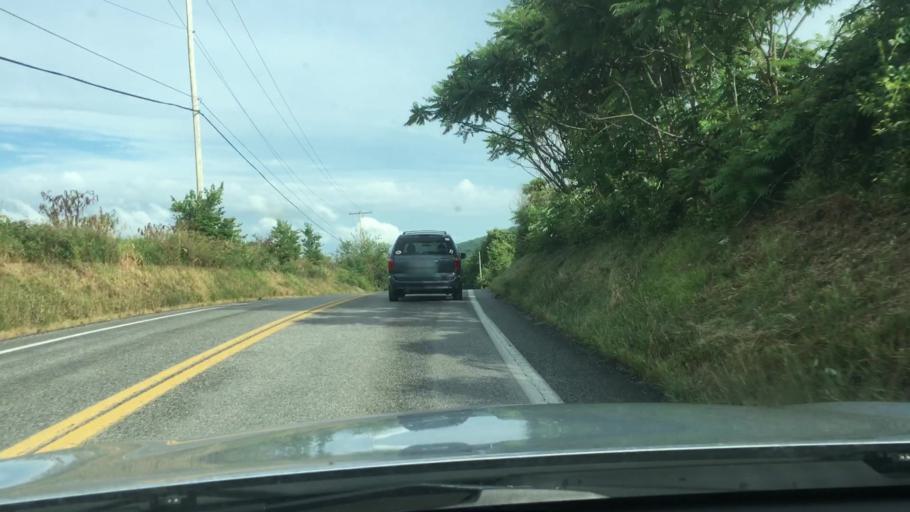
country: US
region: Pennsylvania
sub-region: Cumberland County
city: Boiling Springs
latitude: 40.1527
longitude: -77.0779
